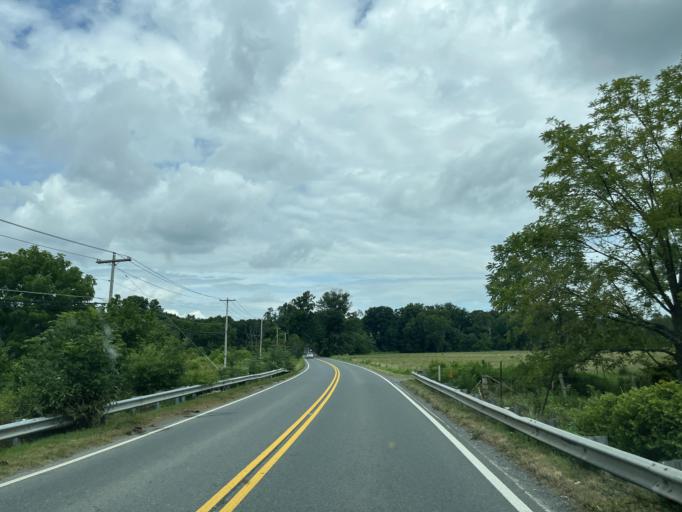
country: US
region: Maryland
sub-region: Montgomery County
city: Montgomery Village
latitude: 39.2333
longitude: -77.1792
